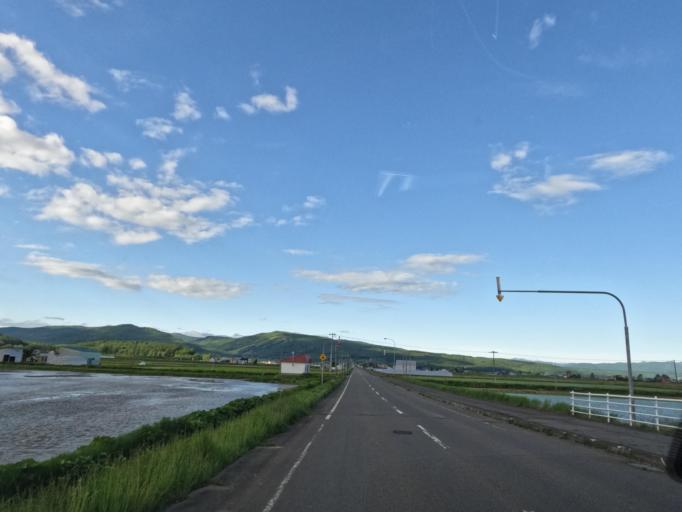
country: JP
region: Hokkaido
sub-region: Asahikawa-shi
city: Asahikawa
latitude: 43.8889
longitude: 142.4641
